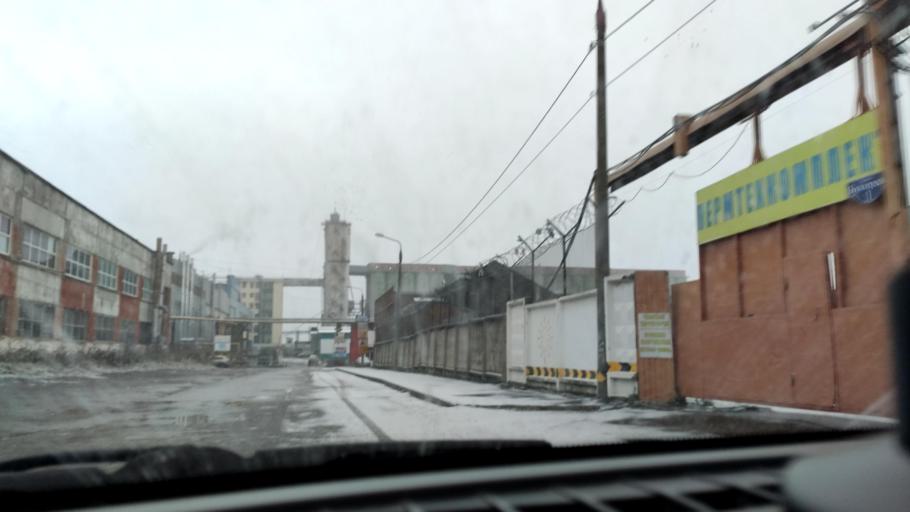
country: RU
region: Perm
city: Perm
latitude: 58.0104
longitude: 56.1865
